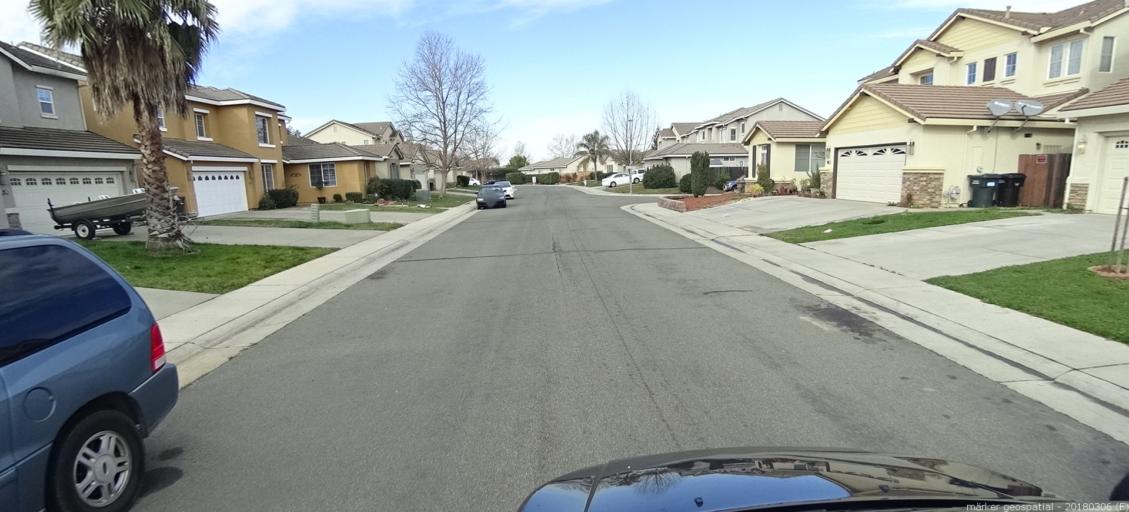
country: US
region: California
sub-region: Sacramento County
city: Vineyard
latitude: 38.4741
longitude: -121.3188
